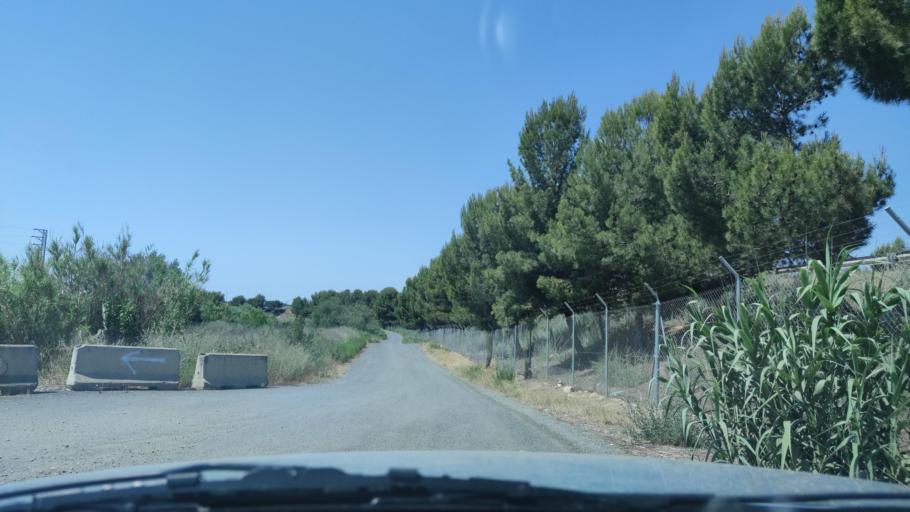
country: ES
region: Catalonia
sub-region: Provincia de Lleida
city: Alpicat
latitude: 41.6495
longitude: 0.5701
